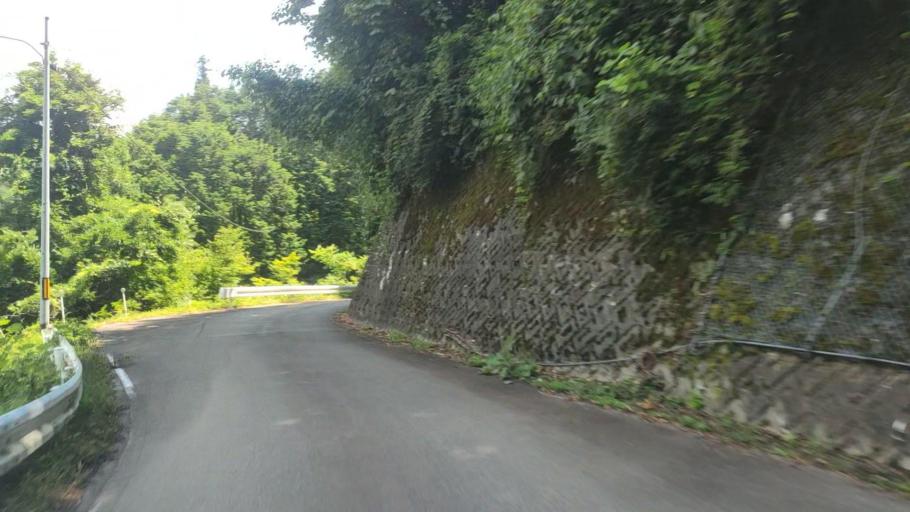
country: JP
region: Fukui
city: Ono
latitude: 35.7174
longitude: 136.5834
